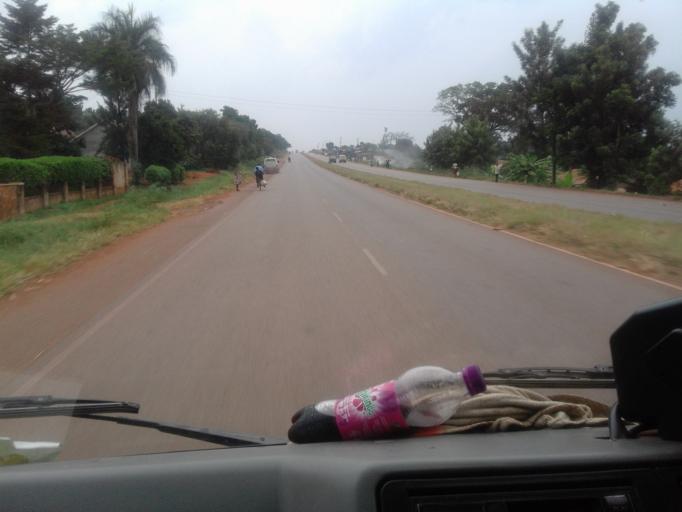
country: UG
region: Eastern Region
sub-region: Jinja District
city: Bugembe
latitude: 0.4684
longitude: 33.2437
